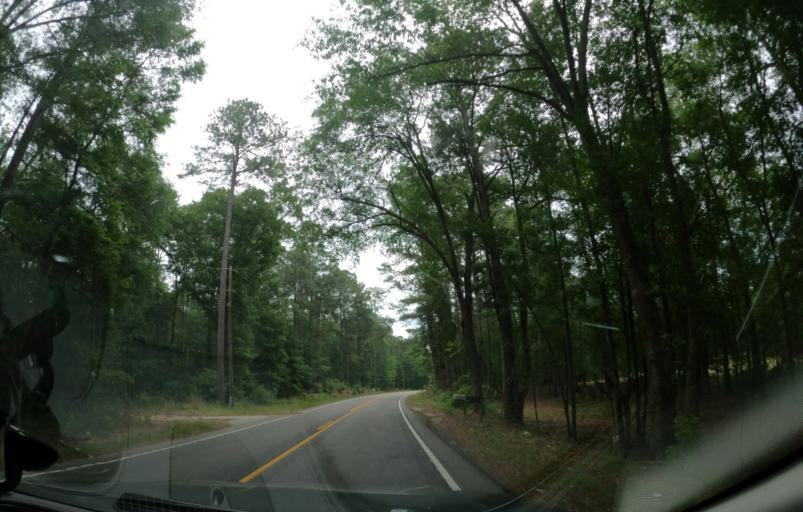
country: US
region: South Carolina
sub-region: Aiken County
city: Aiken
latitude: 33.5742
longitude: -81.6835
